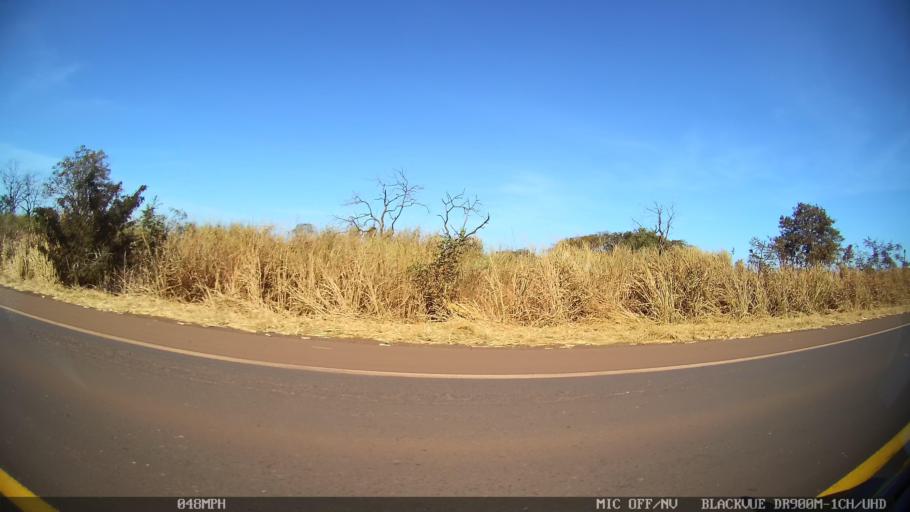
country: BR
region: Sao Paulo
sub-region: Barretos
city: Barretos
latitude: -20.4600
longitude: -48.4655
